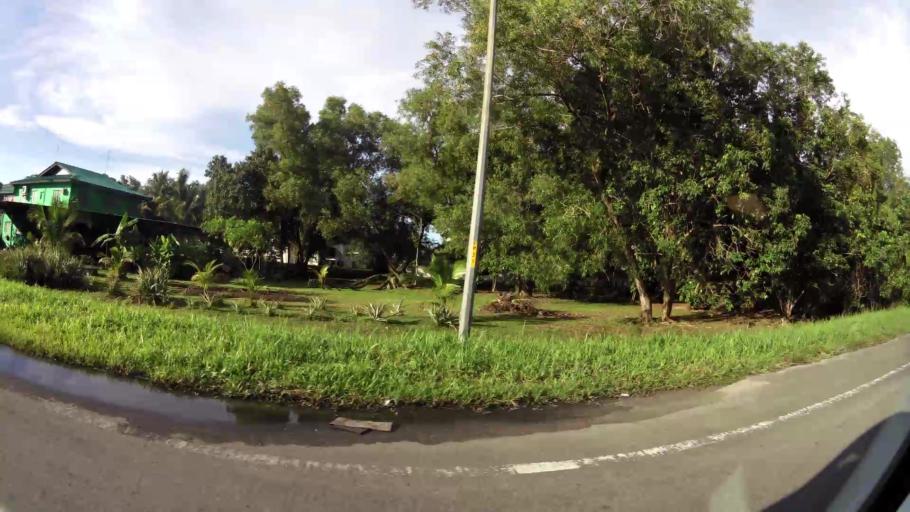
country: BN
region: Brunei and Muara
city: Bandar Seri Begawan
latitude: 4.9708
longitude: 114.9806
